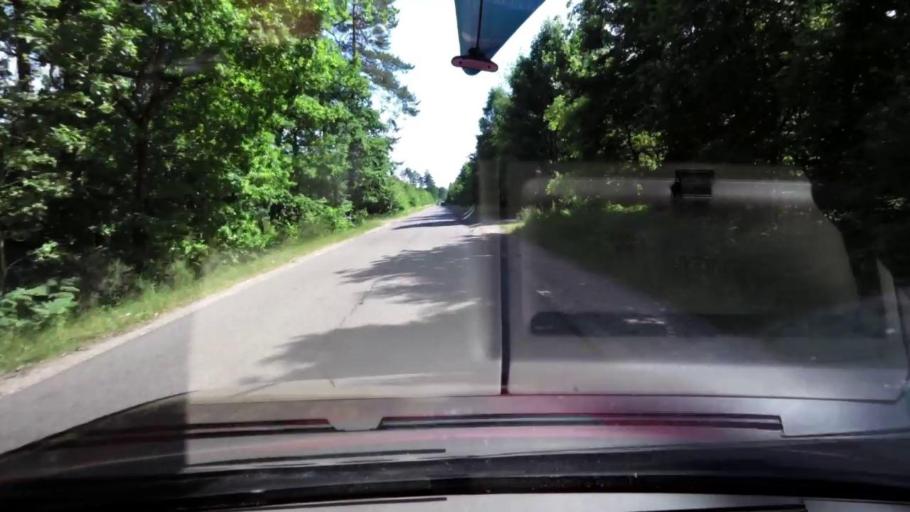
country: PL
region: Pomeranian Voivodeship
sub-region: Powiat slupski
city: Kepice
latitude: 54.3267
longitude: 16.9620
